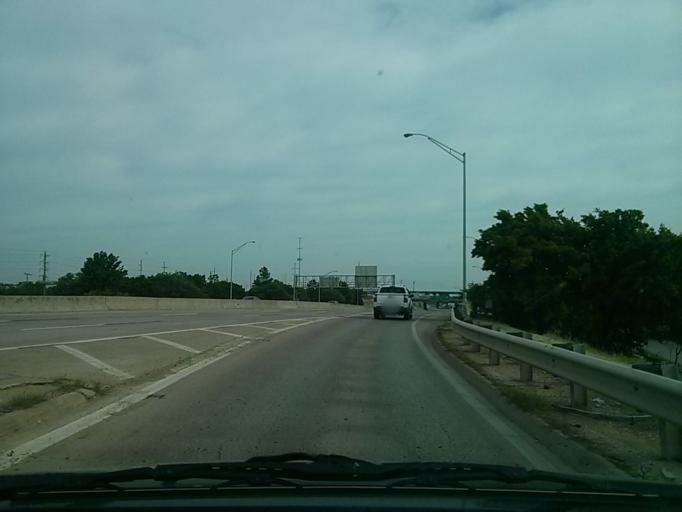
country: US
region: Oklahoma
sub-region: Tulsa County
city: Tulsa
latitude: 36.1522
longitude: -95.9801
